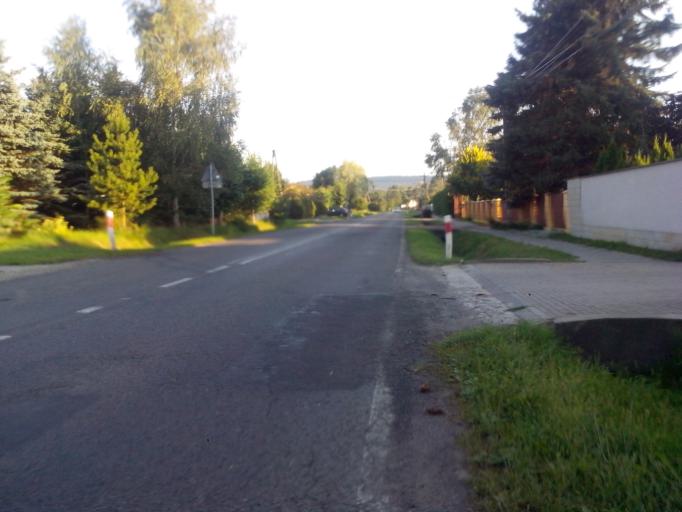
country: PL
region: Subcarpathian Voivodeship
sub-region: Powiat strzyzowski
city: Strzyzow
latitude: 49.8608
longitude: 21.7928
